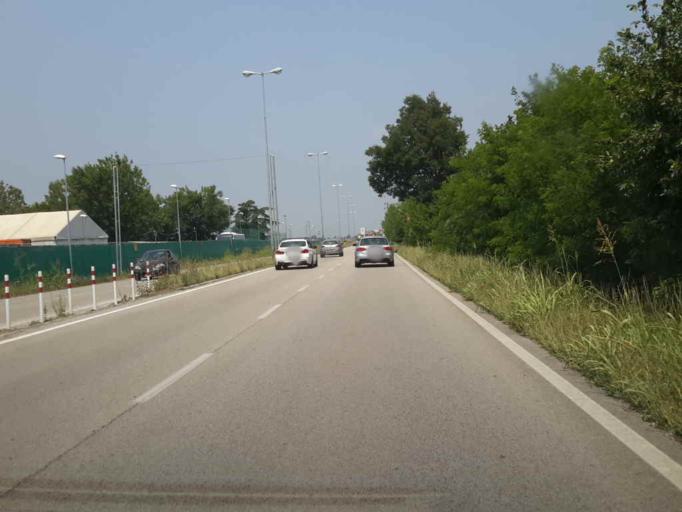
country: IT
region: Veneto
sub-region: Provincia di Vicenza
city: Villaggio Montegrappa
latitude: 45.5472
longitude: 11.5849
